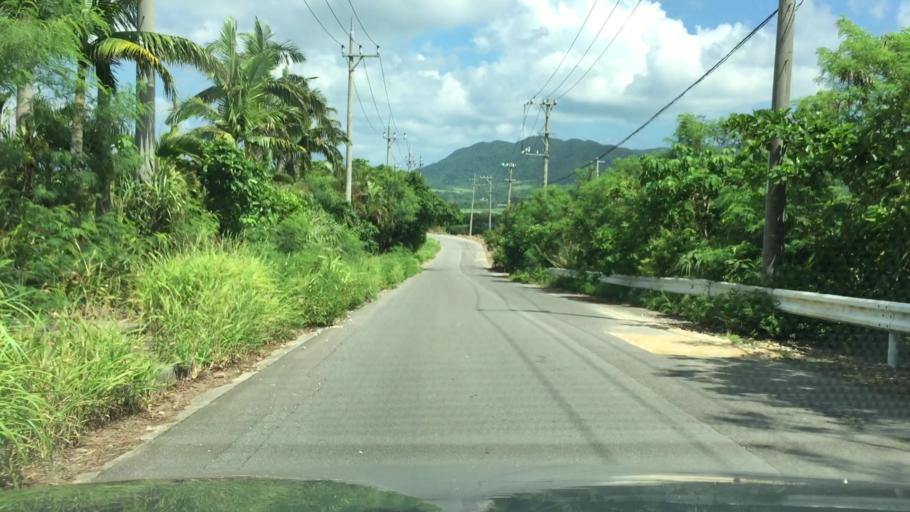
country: JP
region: Okinawa
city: Ishigaki
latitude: 24.3870
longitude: 124.1738
